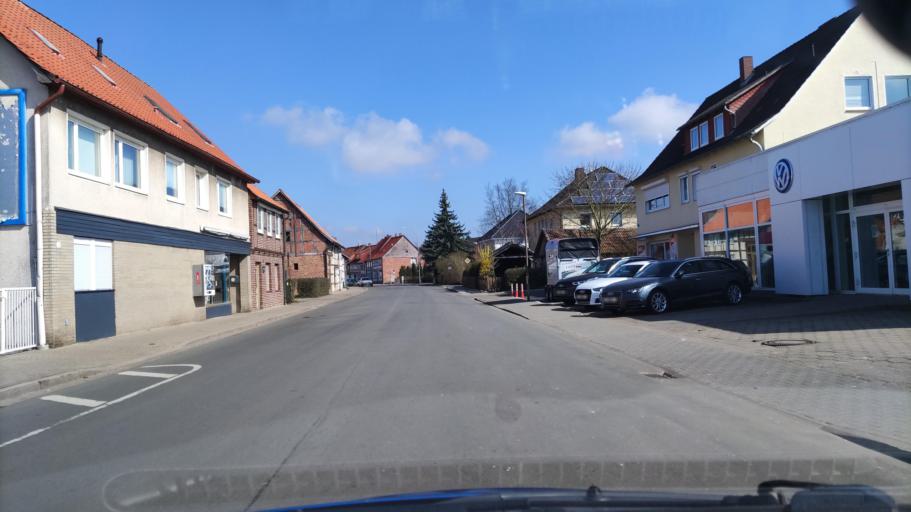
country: DE
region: Lower Saxony
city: Luechow
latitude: 52.9649
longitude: 11.1487
